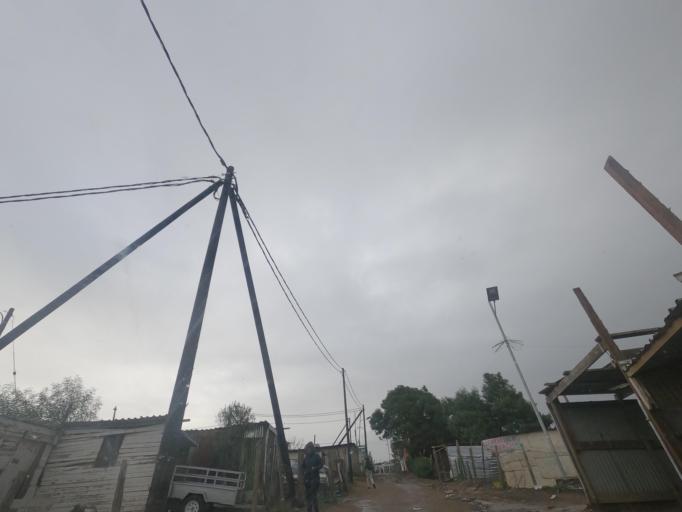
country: ZA
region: Western Cape
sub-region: Cape Winelands District Municipality
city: Stellenbosch
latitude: -33.9253
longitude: 18.8472
